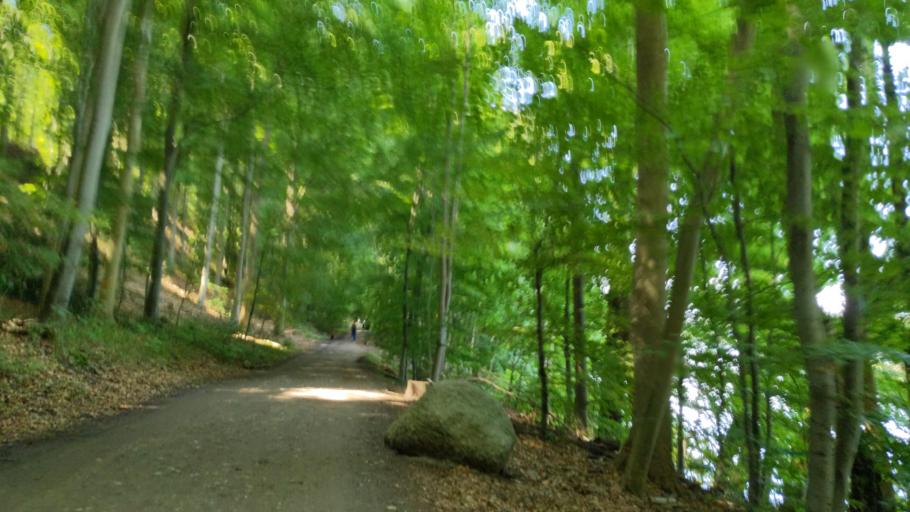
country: DE
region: Schleswig-Holstein
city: Malente
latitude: 54.1592
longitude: 10.5287
